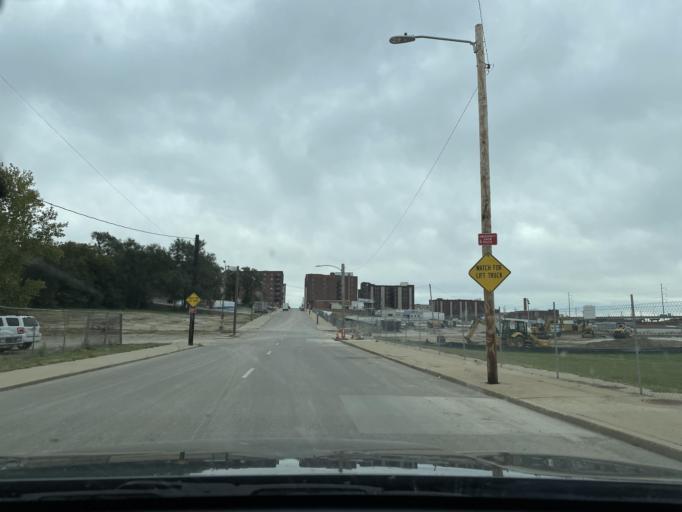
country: US
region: Missouri
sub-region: Buchanan County
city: Saint Joseph
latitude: 39.7727
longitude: -94.8567
